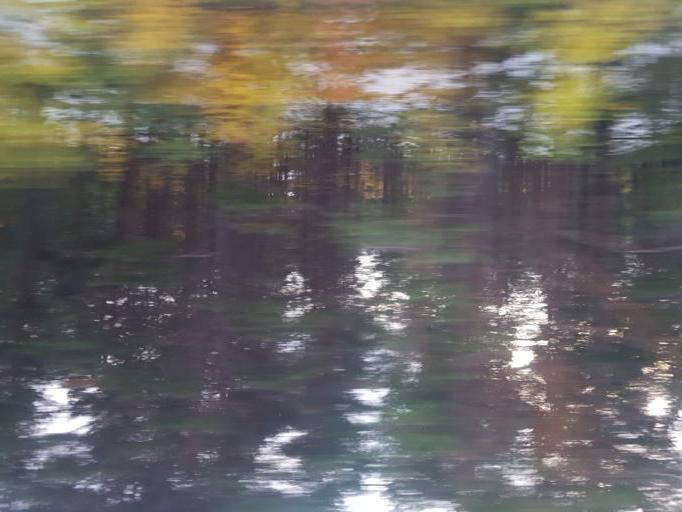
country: NO
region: Oppland
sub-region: Dovre
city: Dombas
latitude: 62.0765
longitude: 9.1280
